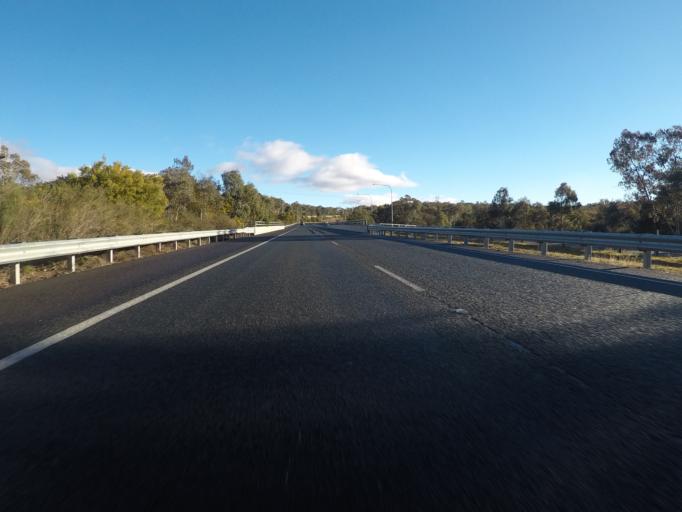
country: AU
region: Australian Capital Territory
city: Macquarie
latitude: -35.2691
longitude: 149.0874
